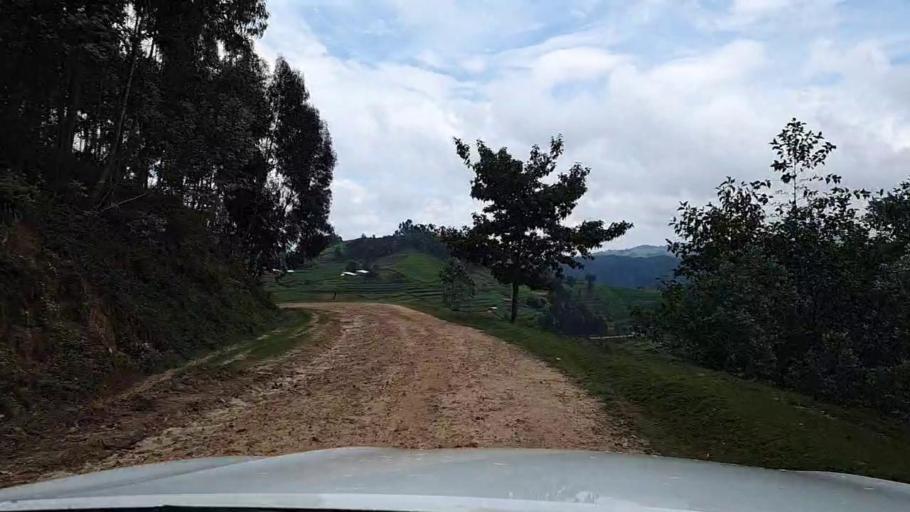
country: RW
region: Western Province
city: Kibuye
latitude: -2.2897
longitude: 29.3719
